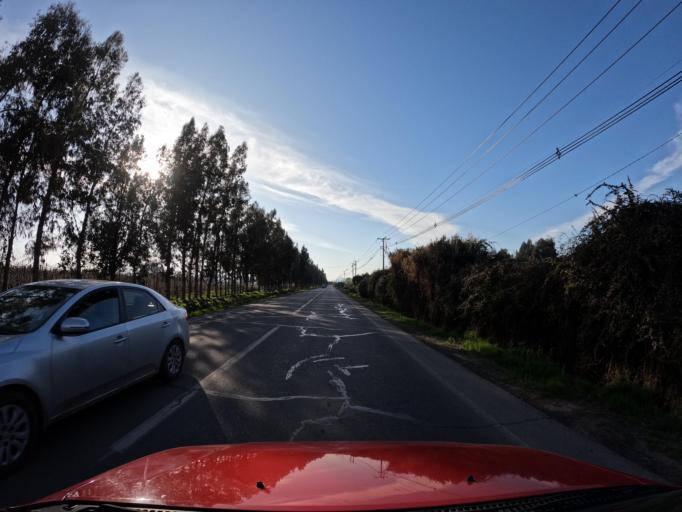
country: CL
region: Maule
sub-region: Provincia de Curico
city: Teno
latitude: -34.8771
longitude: -71.0818
